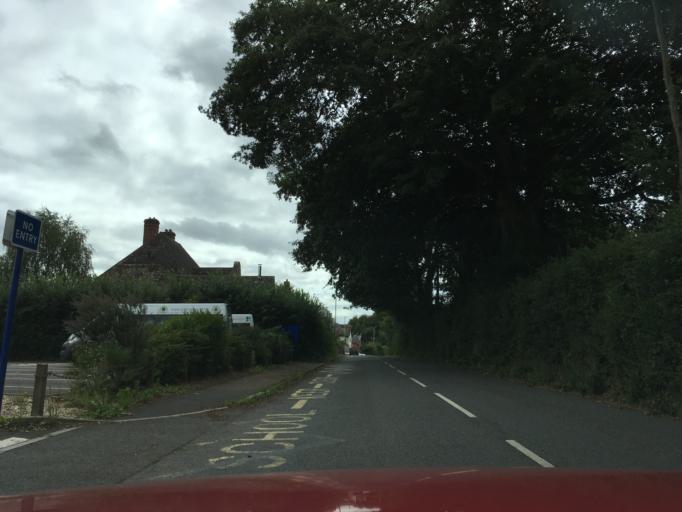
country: GB
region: England
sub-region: Devon
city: Bradninch
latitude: 50.7676
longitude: -3.4426
